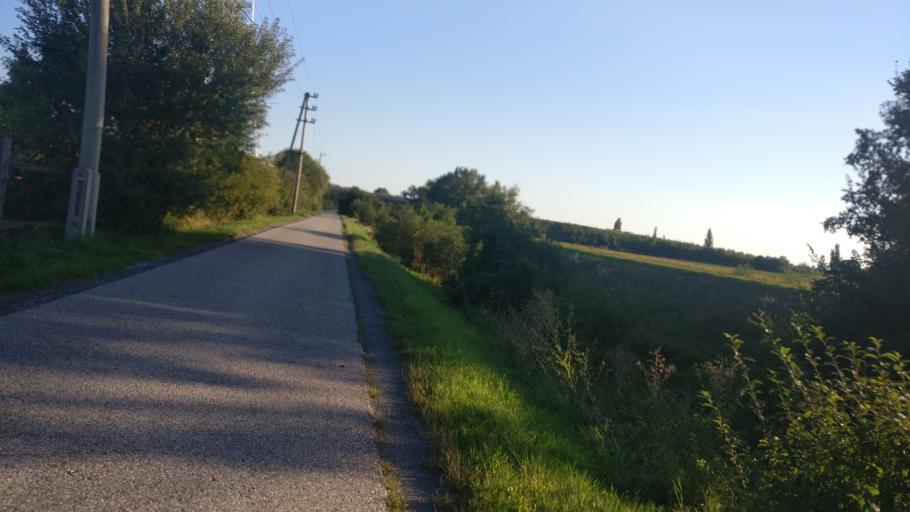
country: AT
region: Lower Austria
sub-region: Politischer Bezirk Wien-Umgebung
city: Lanzendorf
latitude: 48.0976
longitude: 16.4417
